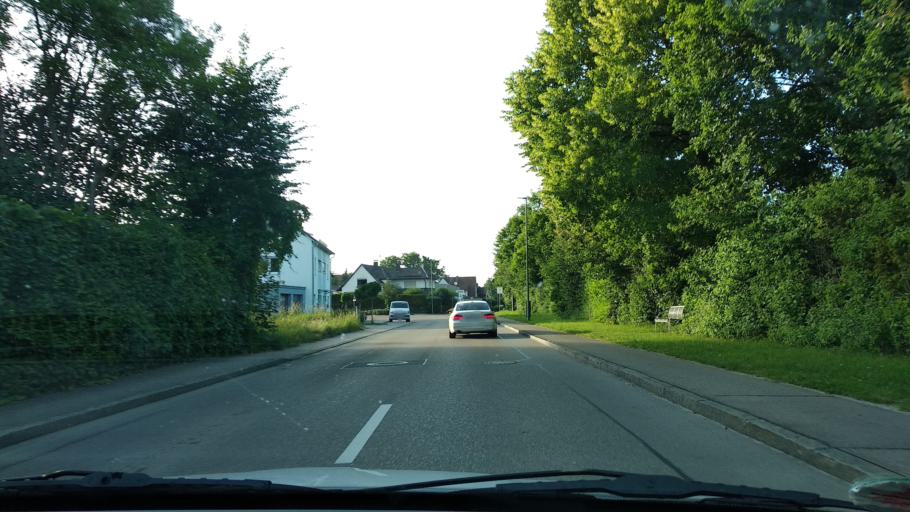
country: DE
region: Bavaria
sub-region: Swabia
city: Altenstadt
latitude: 48.1595
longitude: 10.1101
